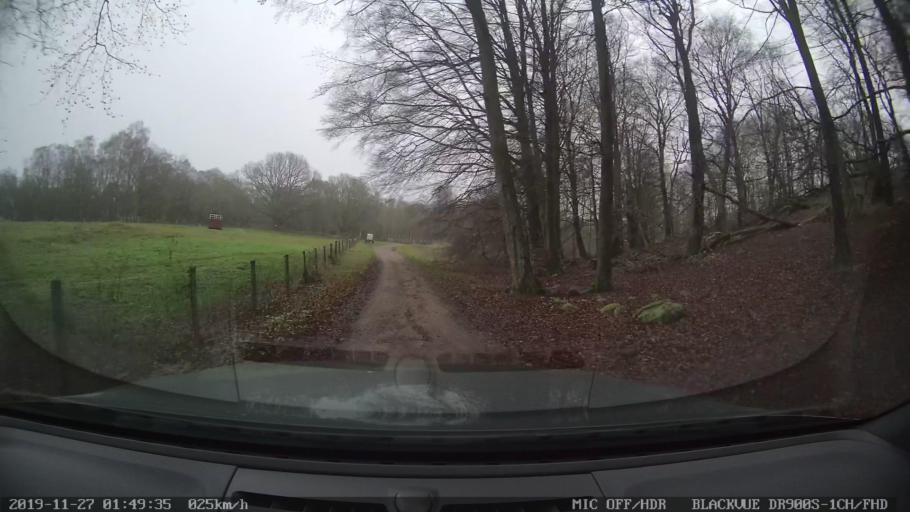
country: SE
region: Skane
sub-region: Hoganas Kommun
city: Hoganas
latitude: 56.2794
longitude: 12.5452
